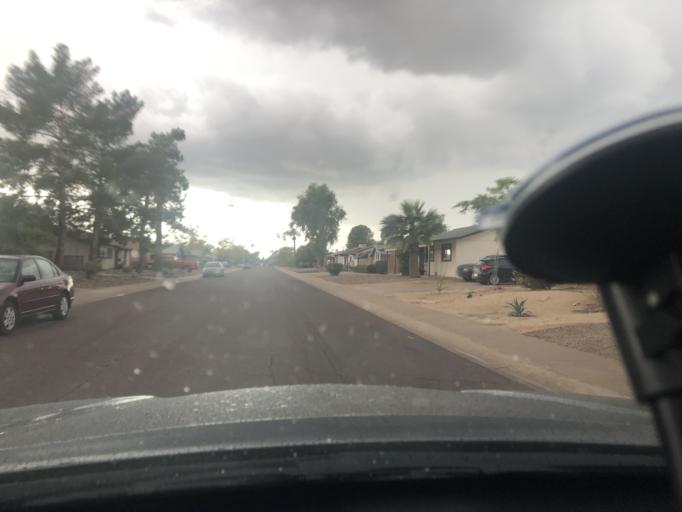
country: US
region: Arizona
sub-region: Maricopa County
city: Scottsdale
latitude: 33.4796
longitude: -111.8934
